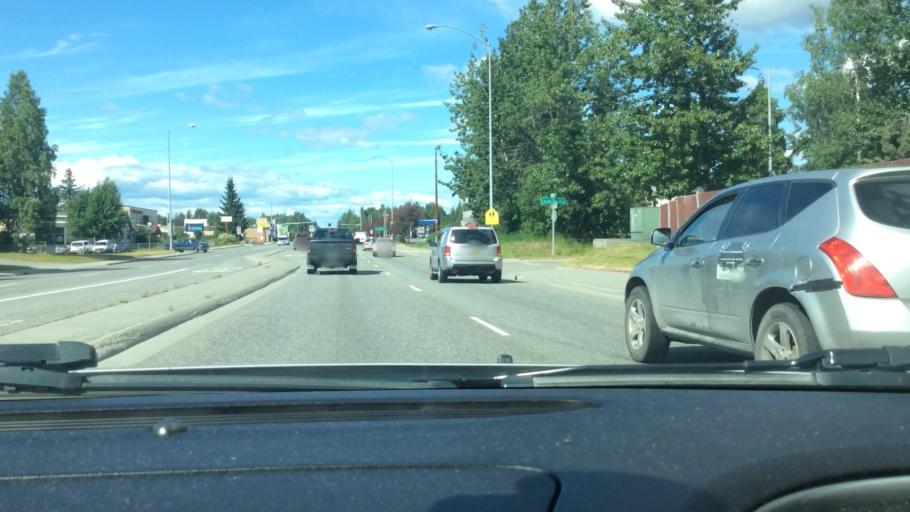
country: US
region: Alaska
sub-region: Anchorage Municipality
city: Anchorage
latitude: 61.1922
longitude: -149.7783
